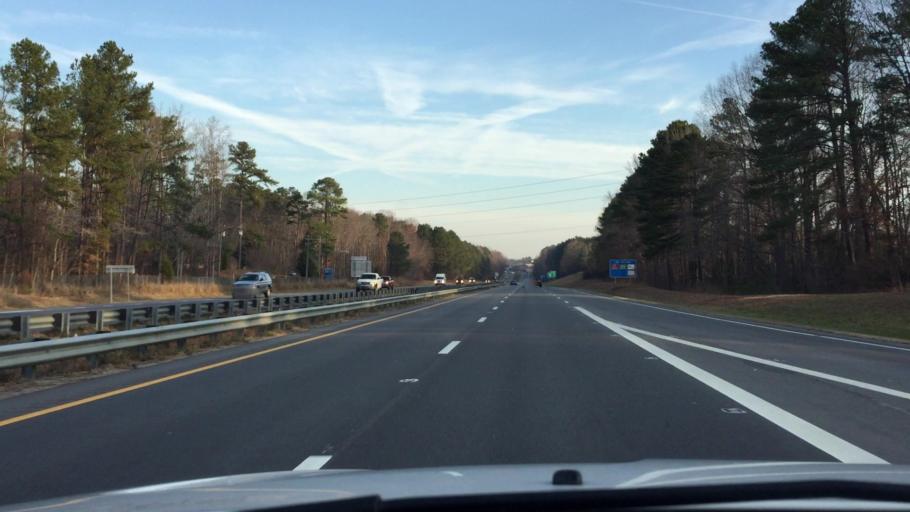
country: US
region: North Carolina
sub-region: Lee County
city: Sanford
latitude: 35.4712
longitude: -79.2021
